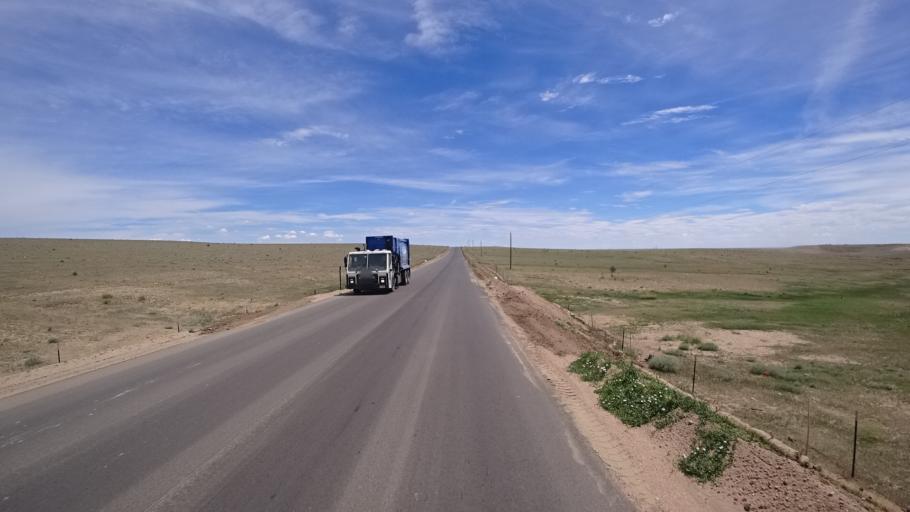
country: US
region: Colorado
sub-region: El Paso County
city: Fountain
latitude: 38.6940
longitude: -104.6482
